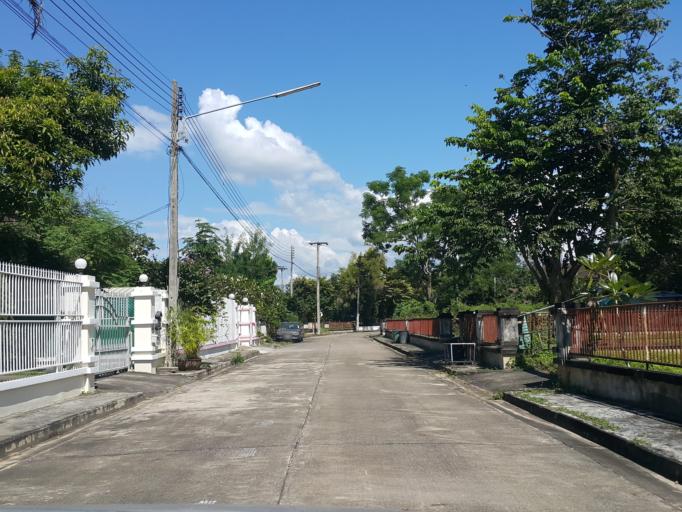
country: TH
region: Chiang Mai
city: San Sai
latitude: 18.8474
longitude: 99.0043
